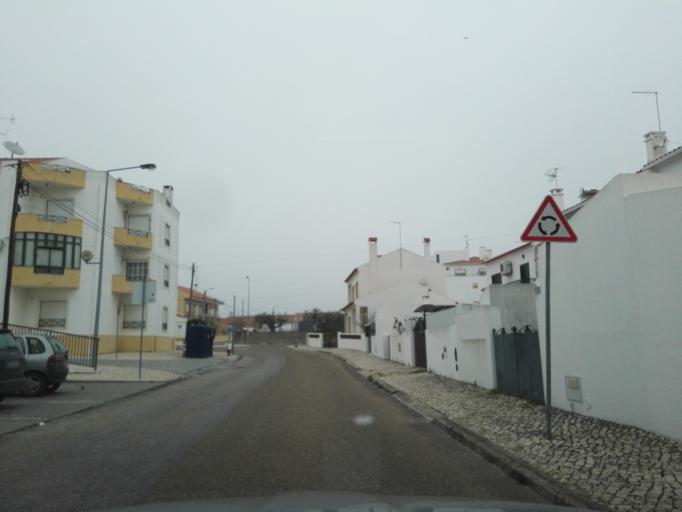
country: PT
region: Evora
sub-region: Vendas Novas
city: Vendas Novas
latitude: 38.6752
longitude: -8.4538
